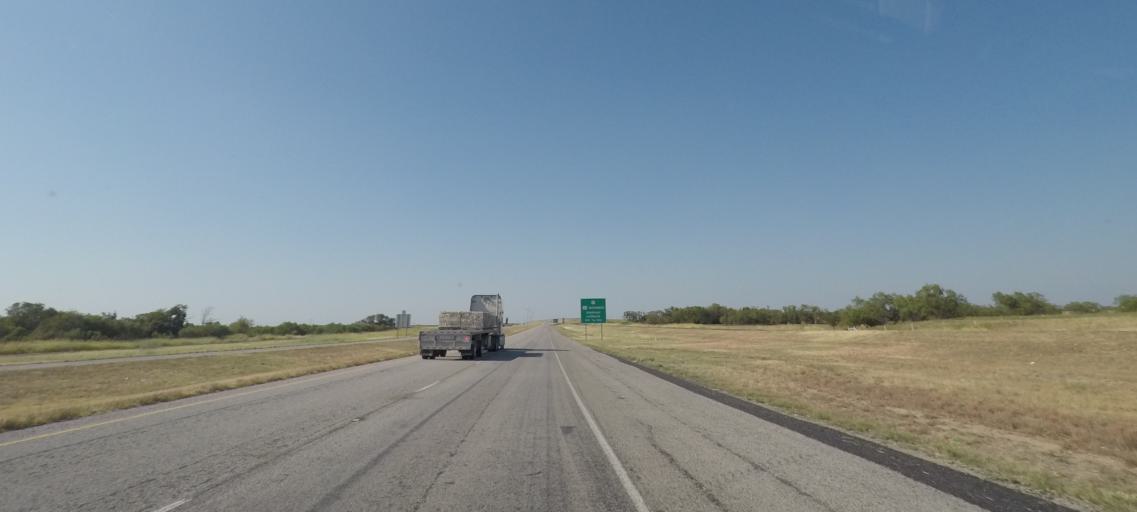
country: US
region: Texas
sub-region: Baylor County
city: Seymour
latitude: 33.6046
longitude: -99.2421
